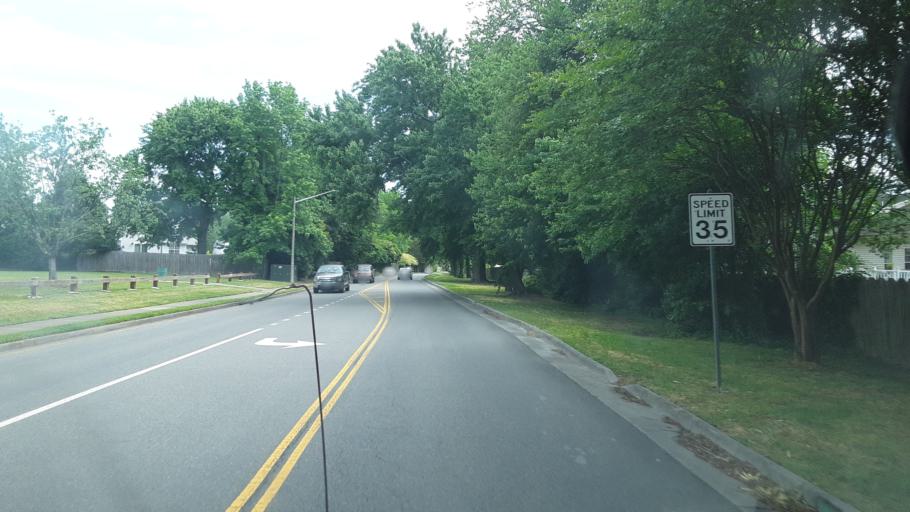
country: US
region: Virginia
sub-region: City of Virginia Beach
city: Virginia Beach
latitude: 36.7662
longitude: -76.0014
